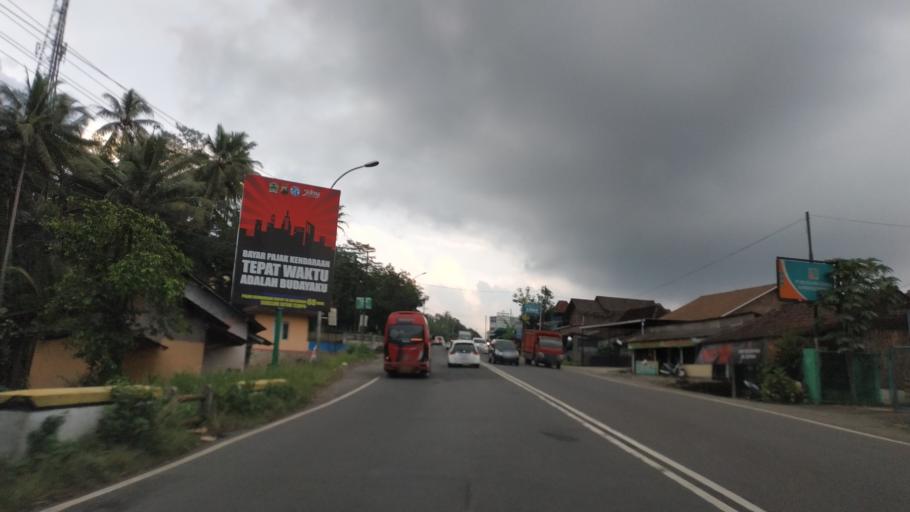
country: ID
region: Central Java
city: Salatiga
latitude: -7.2889
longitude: 110.4646
